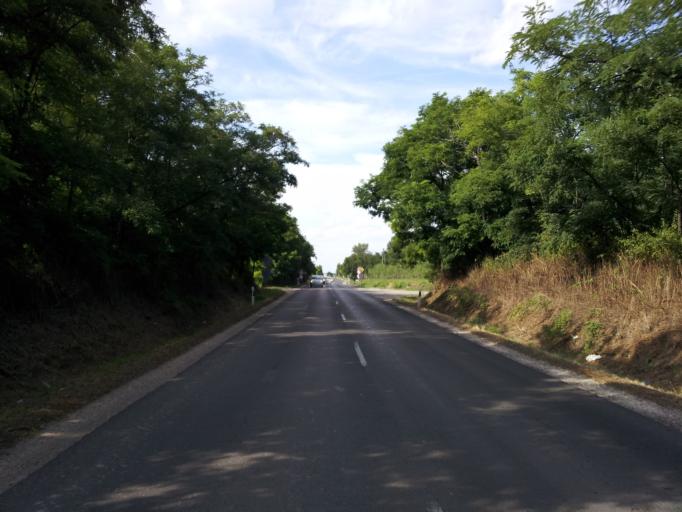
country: HU
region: Pest
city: Kiskunlachaza
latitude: 47.2126
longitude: 19.0166
